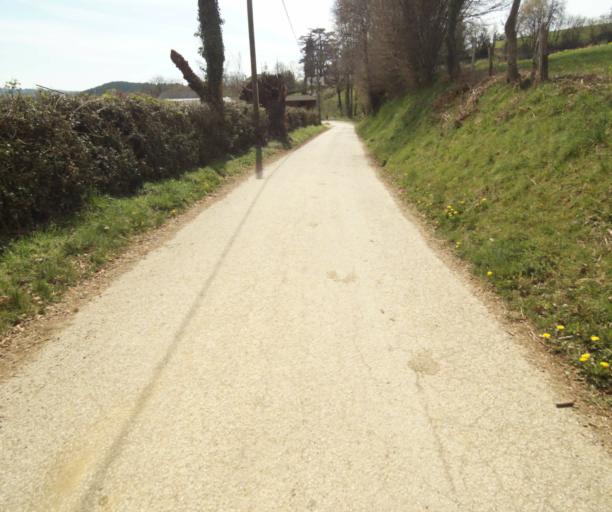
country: FR
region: Limousin
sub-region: Departement de la Correze
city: Naves
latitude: 45.3518
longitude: 1.7982
